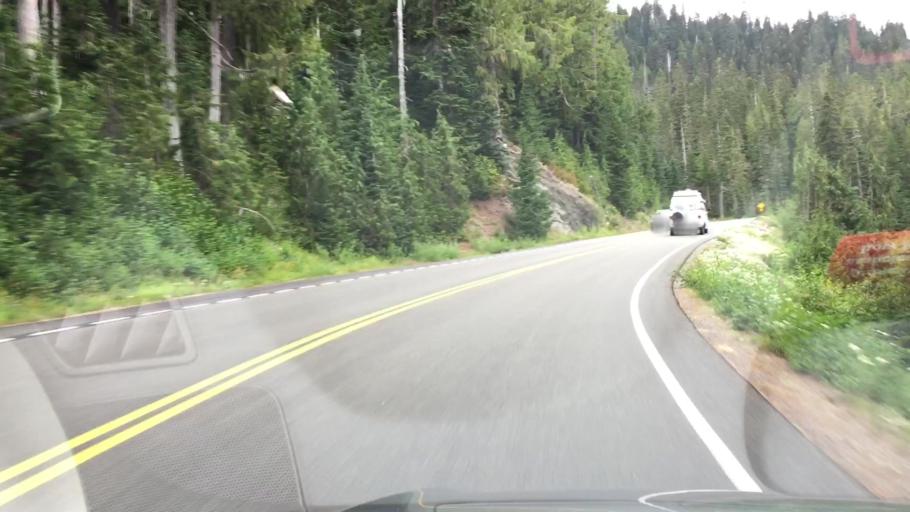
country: US
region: Washington
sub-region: Pierce County
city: Buckley
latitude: 46.7772
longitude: -121.7453
